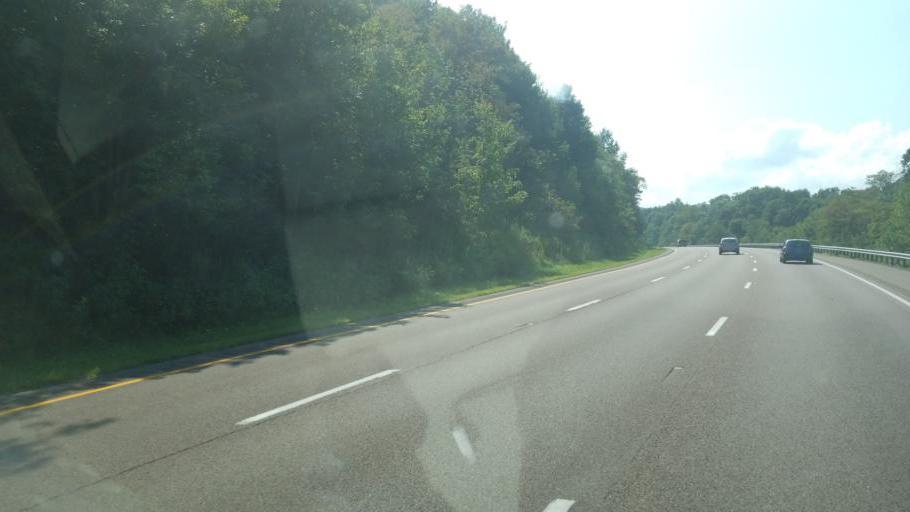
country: US
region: Maryland
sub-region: Allegany County
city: Frostburg
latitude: 39.6421
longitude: -78.8711
